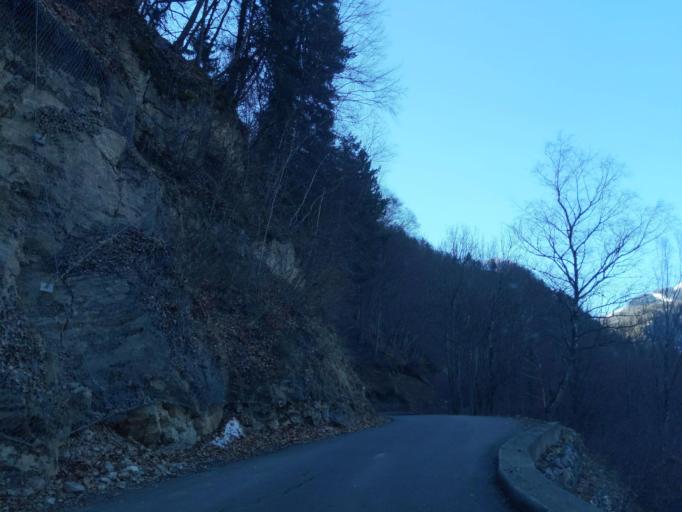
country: FR
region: Rhone-Alpes
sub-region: Departement de la Savoie
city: Salins-les-Thermes
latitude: 45.4505
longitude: 6.5133
